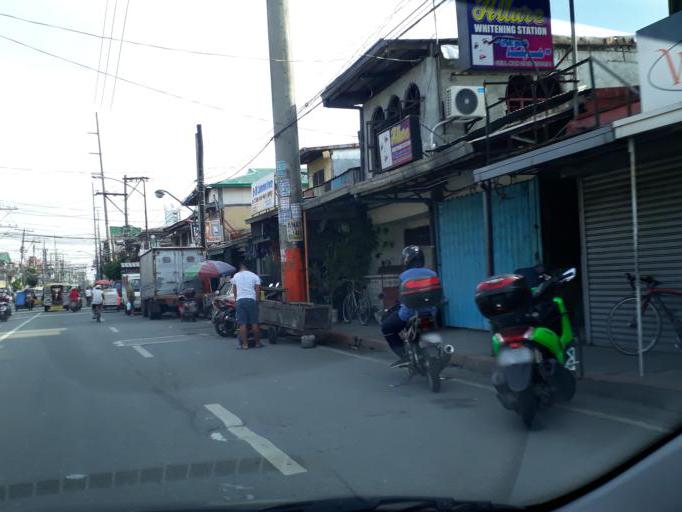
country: PH
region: Metro Manila
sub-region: City of Manila
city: Manila
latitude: 14.6317
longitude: 120.9745
